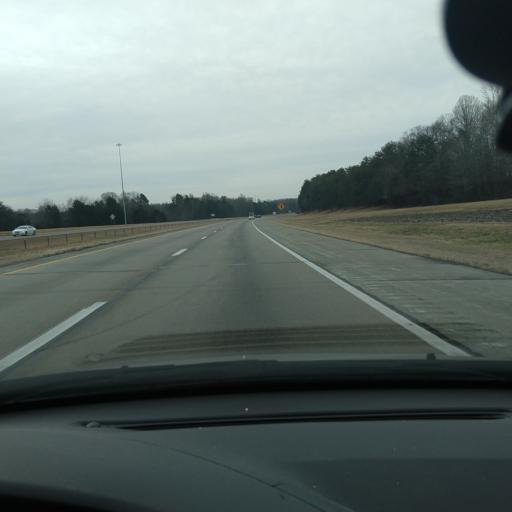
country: US
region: North Carolina
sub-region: Davidson County
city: Midway
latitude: 35.9688
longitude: -80.2298
